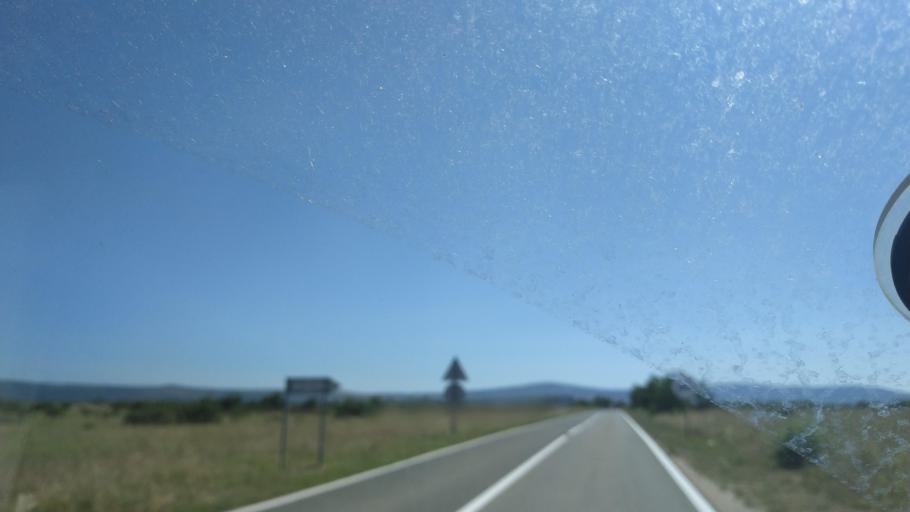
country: HR
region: Sibensko-Kniniska
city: Drnis
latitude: 43.8144
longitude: 16.0523
